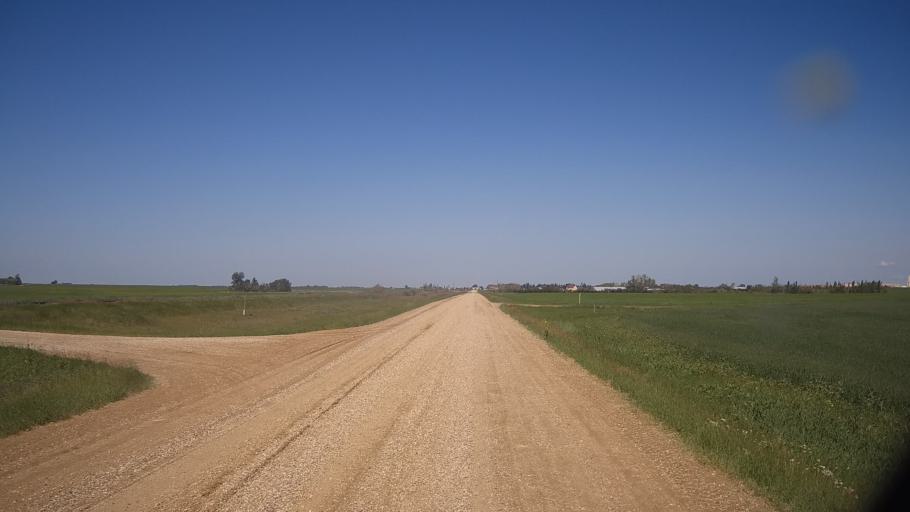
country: CA
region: Saskatchewan
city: Watrous
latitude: 51.8824
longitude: -106.0265
